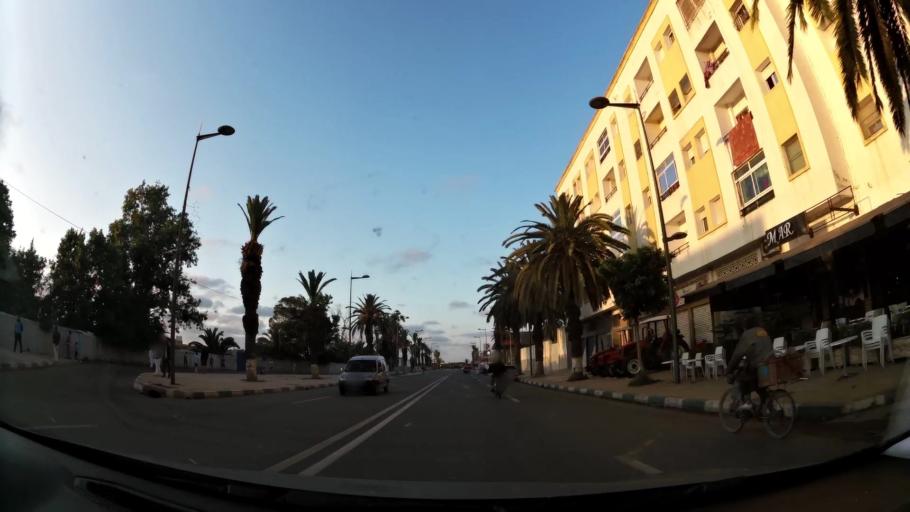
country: MA
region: Gharb-Chrarda-Beni Hssen
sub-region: Kenitra Province
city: Kenitra
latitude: 34.2737
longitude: -6.5570
